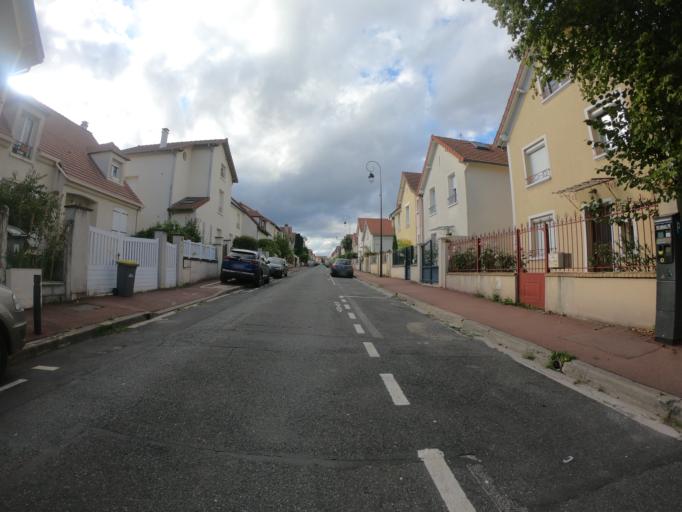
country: FR
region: Ile-de-France
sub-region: Departement des Hauts-de-Seine
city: Antony
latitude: 48.7571
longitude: 2.2971
